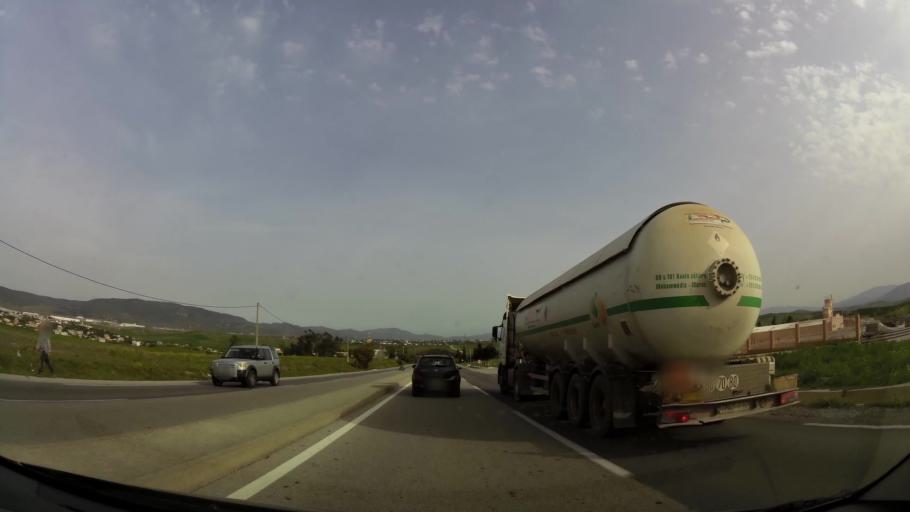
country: MA
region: Tanger-Tetouan
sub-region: Tanger-Assilah
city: Dar Chaoui
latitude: 35.6583
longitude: -5.6939
